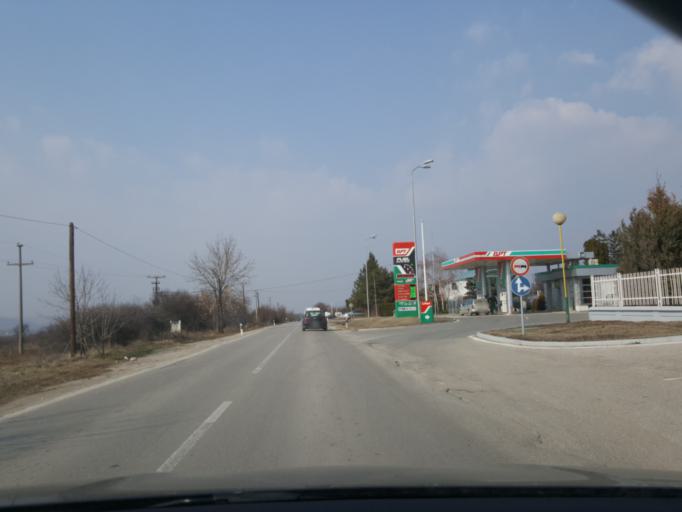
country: RS
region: Central Serbia
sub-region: Nisavski Okrug
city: Nis
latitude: 43.3872
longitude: 21.8173
